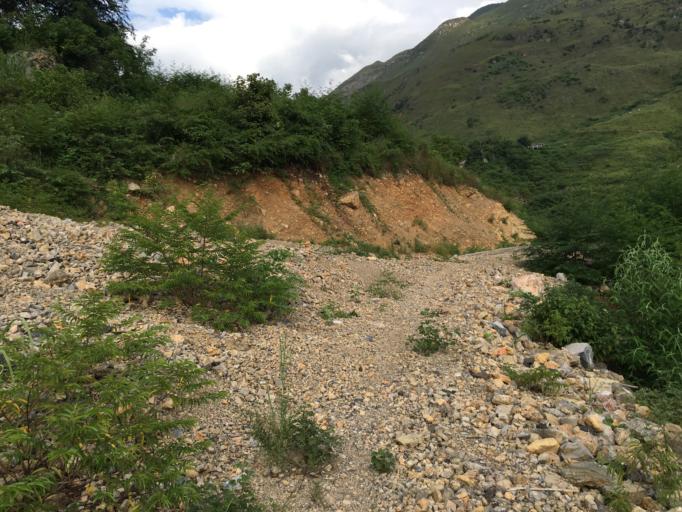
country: CN
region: Guizhou Sheng
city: Anshun
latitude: 25.7782
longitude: 105.3903
